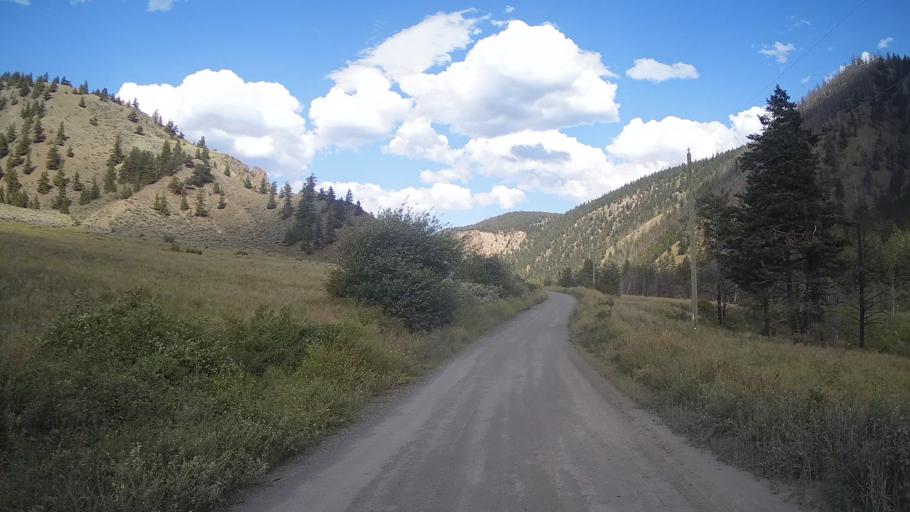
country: CA
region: British Columbia
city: Lillooet
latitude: 51.2204
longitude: -122.0802
